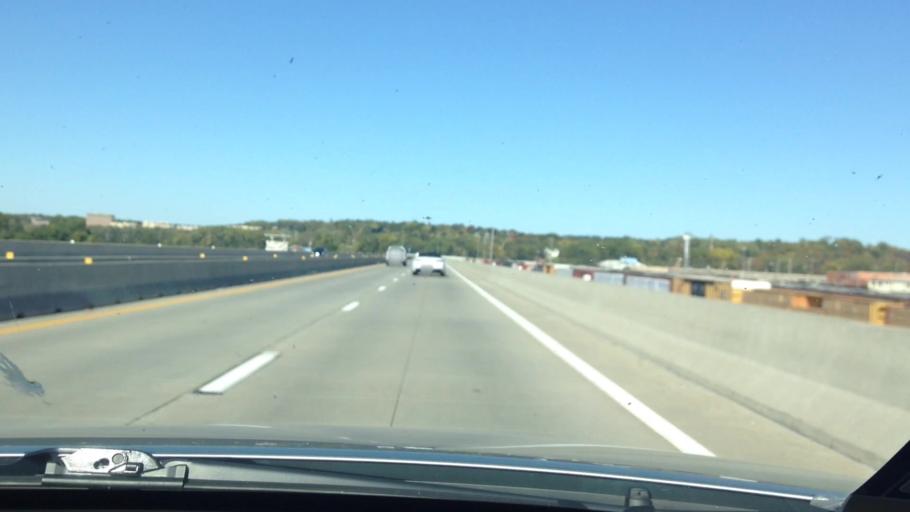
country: US
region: Missouri
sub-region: Clay County
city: North Kansas City
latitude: 39.1428
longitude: -94.5867
